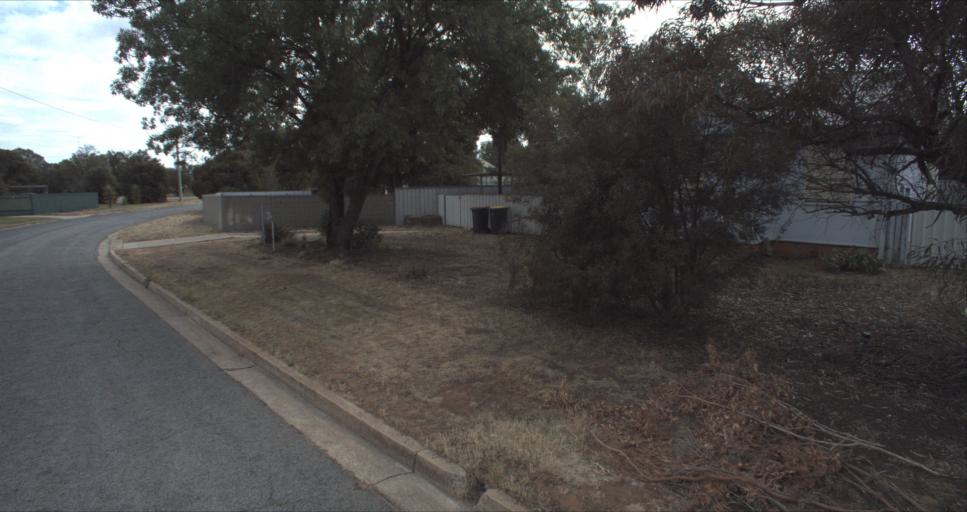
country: AU
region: New South Wales
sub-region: Leeton
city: Leeton
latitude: -34.5647
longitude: 146.3939
